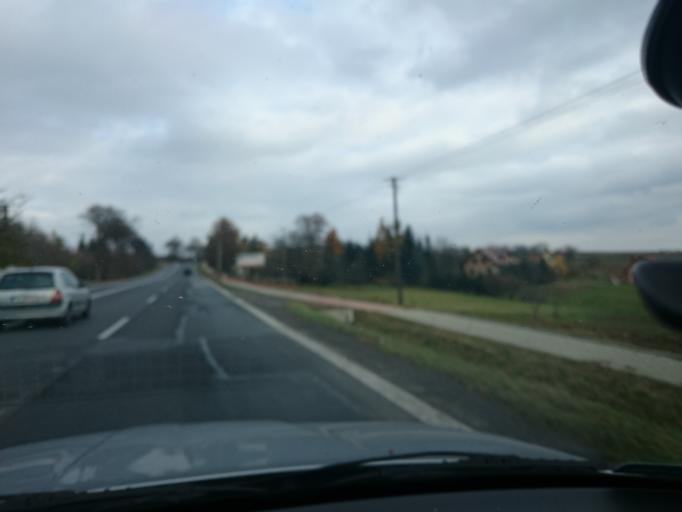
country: PL
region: Lesser Poland Voivodeship
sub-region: Powiat krakowski
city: Michalowice
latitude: 50.1776
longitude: 19.9893
